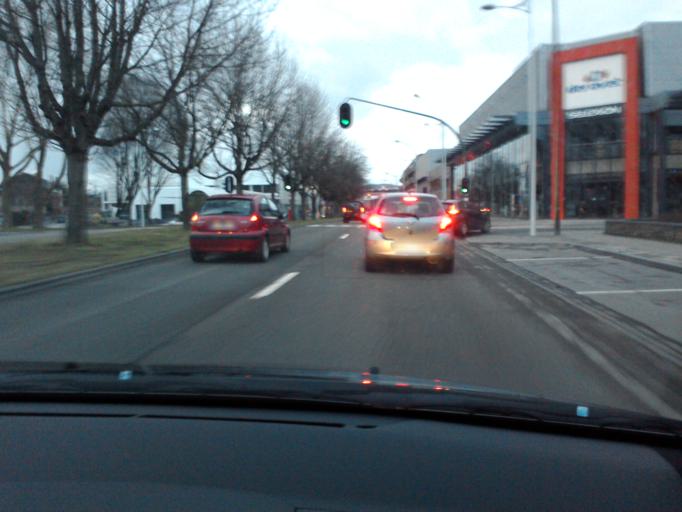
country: BE
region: Wallonia
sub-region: Province de Liege
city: Liege
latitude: 50.6263
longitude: 5.5891
